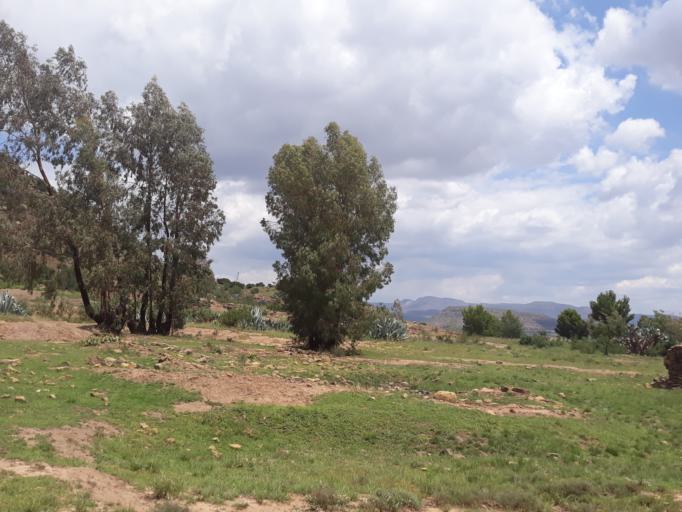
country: LS
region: Quthing
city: Quthing
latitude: -30.3404
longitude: 27.5328
